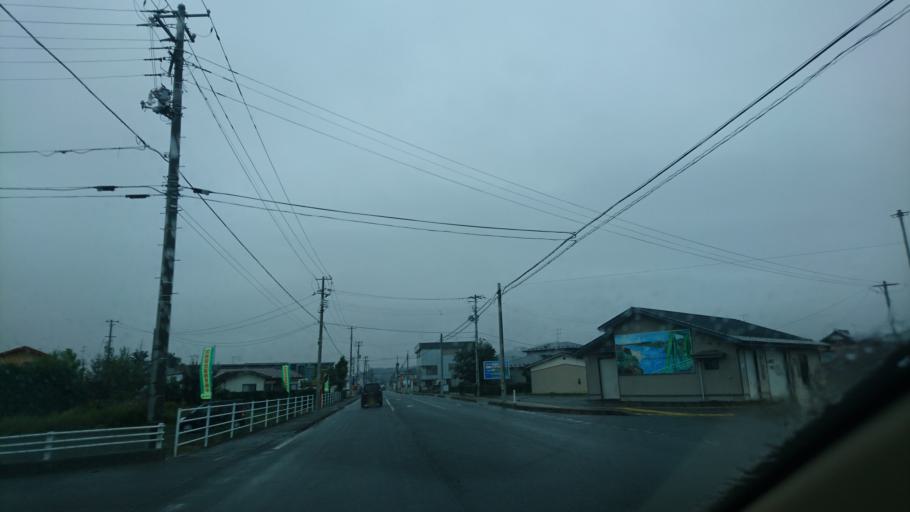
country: JP
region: Iwate
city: Mizusawa
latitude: 39.1382
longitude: 141.1782
